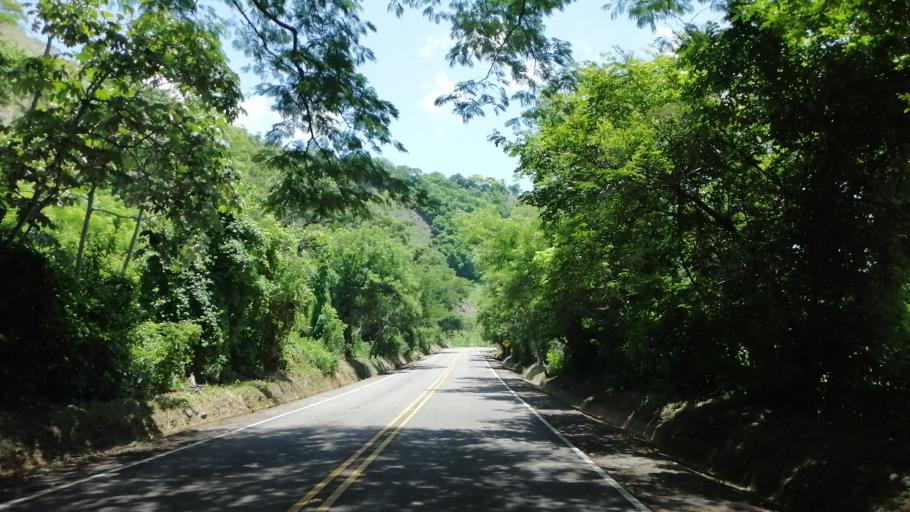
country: SV
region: Chalatenango
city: Nueva Concepcion
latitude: 14.1729
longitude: -89.3120
